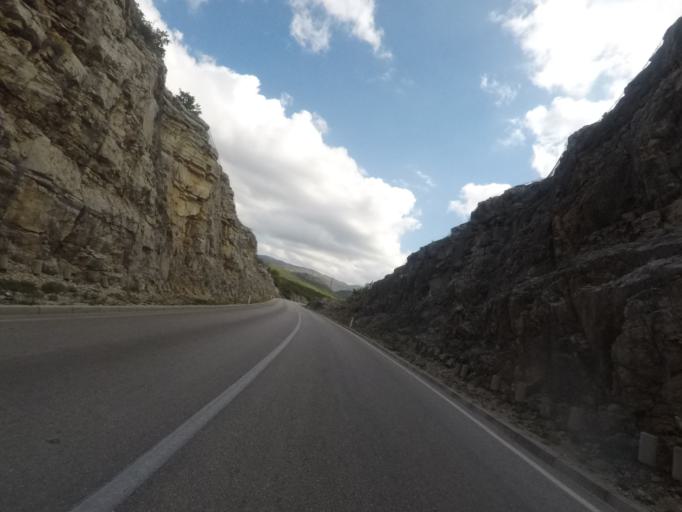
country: BA
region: Republika Srpska
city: Trebinje
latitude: 42.6489
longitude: 18.3708
